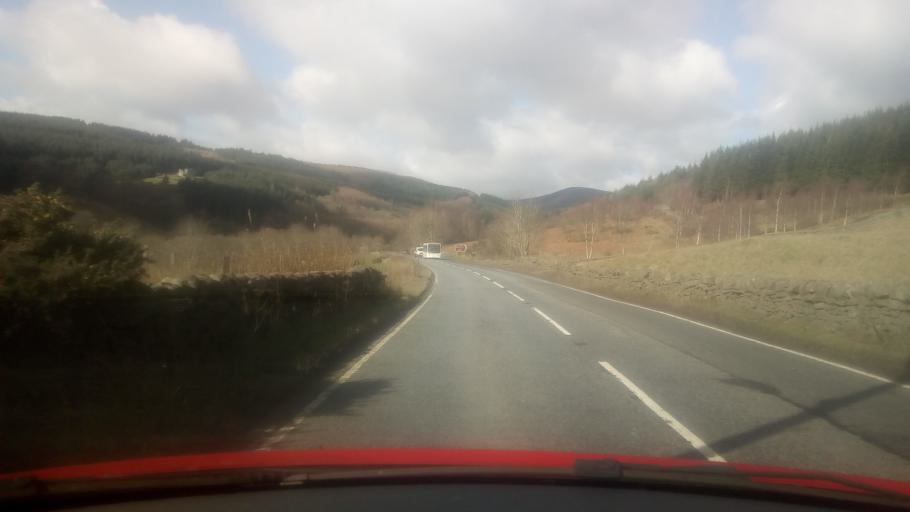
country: GB
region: Scotland
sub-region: The Scottish Borders
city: Innerleithen
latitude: 55.6169
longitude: -2.9439
